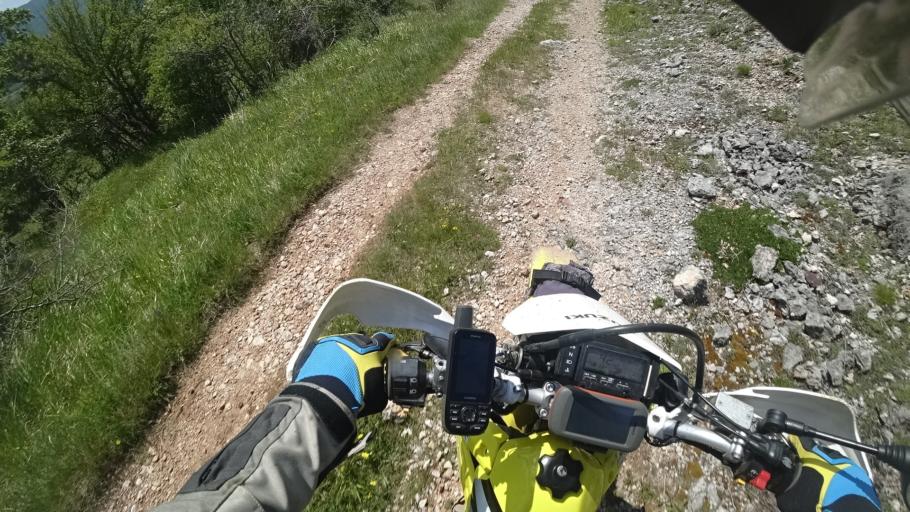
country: HR
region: Zadarska
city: Gracac
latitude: 44.3672
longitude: 15.9510
